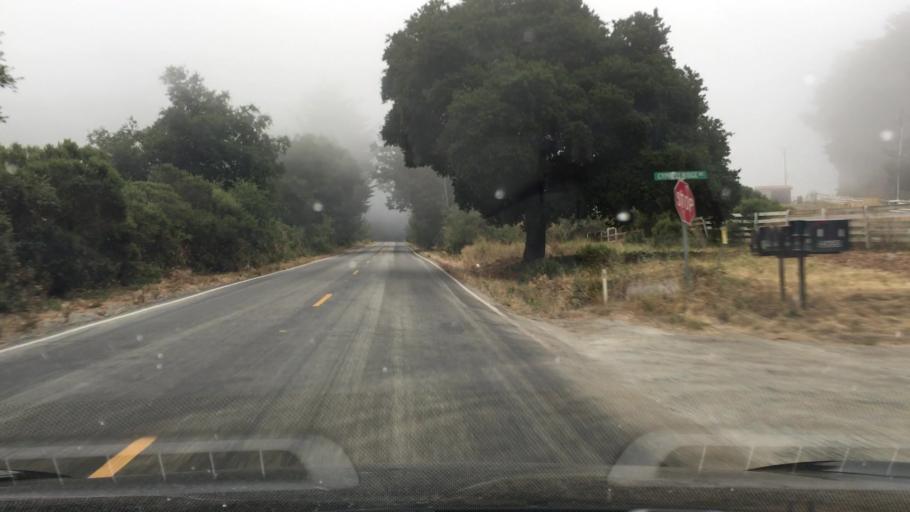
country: US
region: California
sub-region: San Mateo County
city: Highlands-Baywood Park
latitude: 37.4598
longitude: -122.3420
